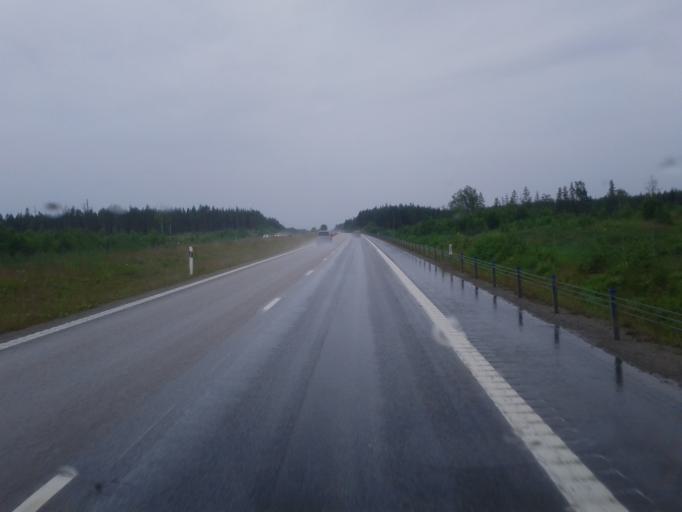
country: SE
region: Uppsala
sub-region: Tierps Kommun
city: Tierp
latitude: 60.2383
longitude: 17.5020
